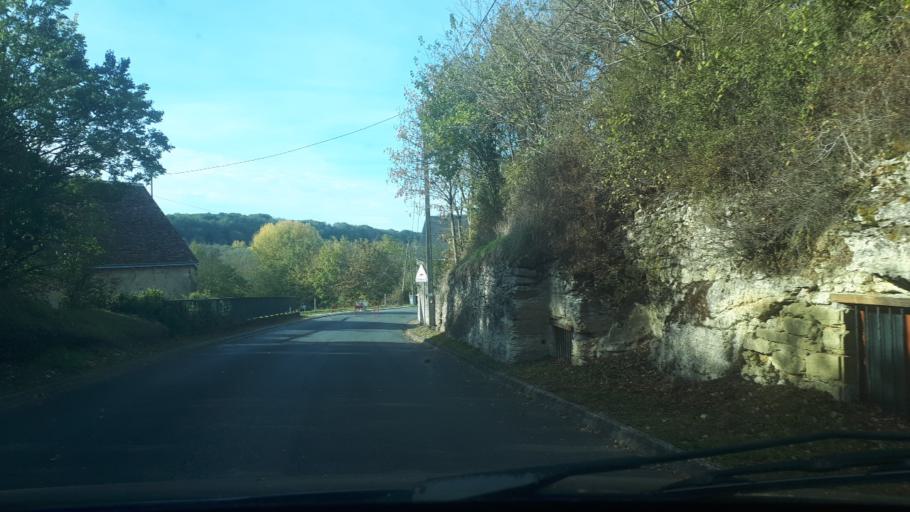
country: FR
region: Centre
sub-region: Departement du Loir-et-Cher
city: Villiers-sur-Loir
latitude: 47.7847
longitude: 0.9651
